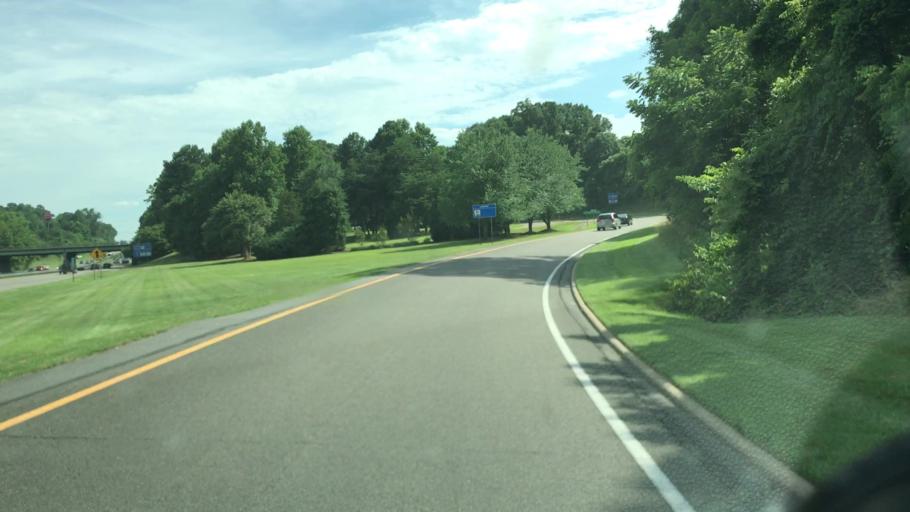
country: US
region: North Carolina
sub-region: Iredell County
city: Statesville
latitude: 35.7937
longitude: -80.8626
